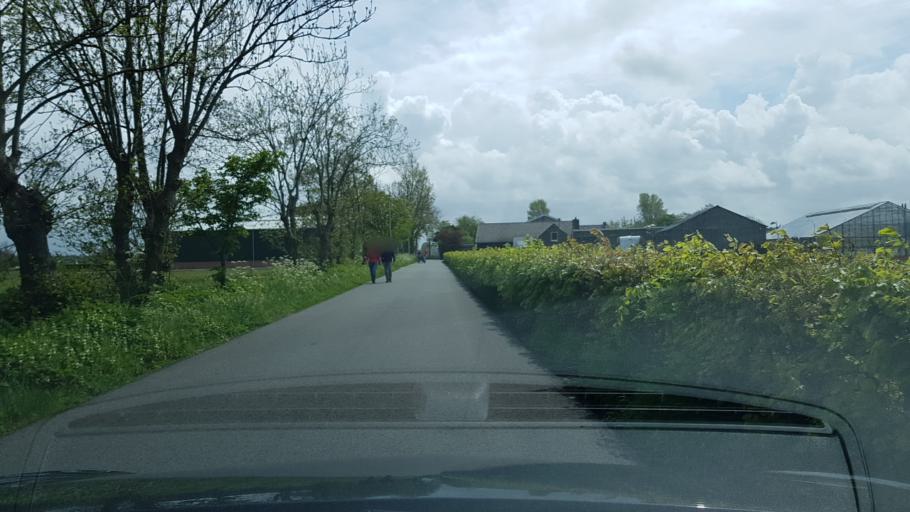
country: NL
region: South Holland
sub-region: Gemeente Teylingen
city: Sassenheim
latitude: 52.2474
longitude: 4.5332
